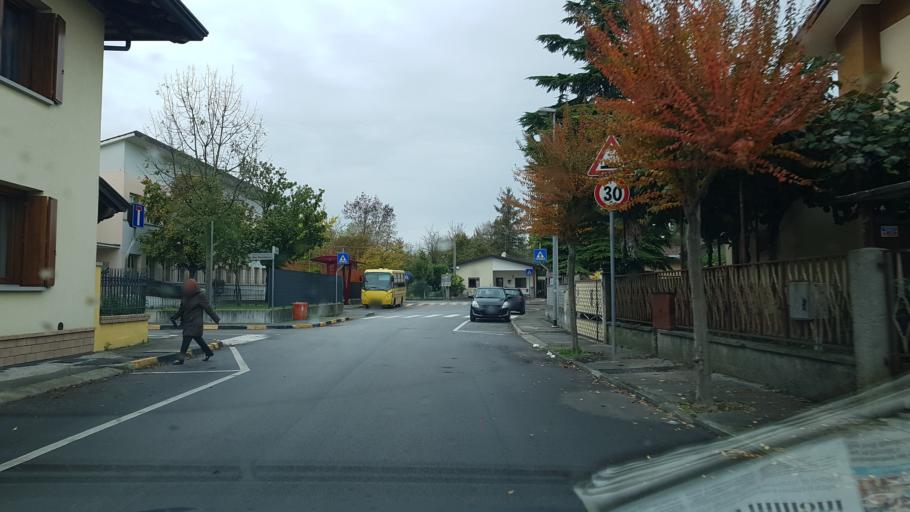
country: IT
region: Friuli Venezia Giulia
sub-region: Provincia di Gorizia
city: San Pier d'Isonzo
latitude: 45.8478
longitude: 13.4572
